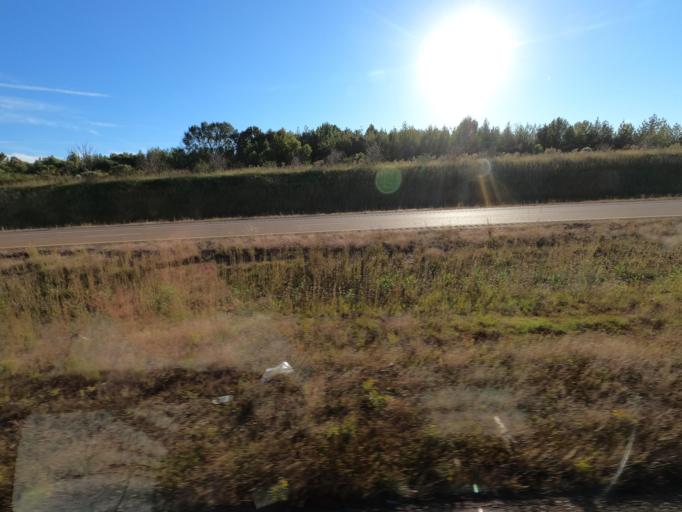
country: US
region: Tennessee
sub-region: Shelby County
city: Collierville
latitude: 35.0731
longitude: -89.6469
